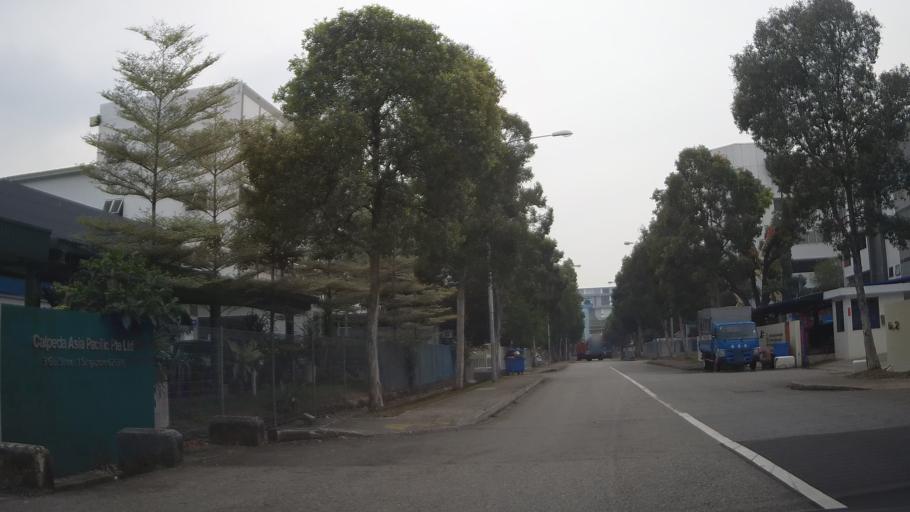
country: MY
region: Johor
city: Johor Bahru
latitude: 1.3192
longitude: 103.6687
